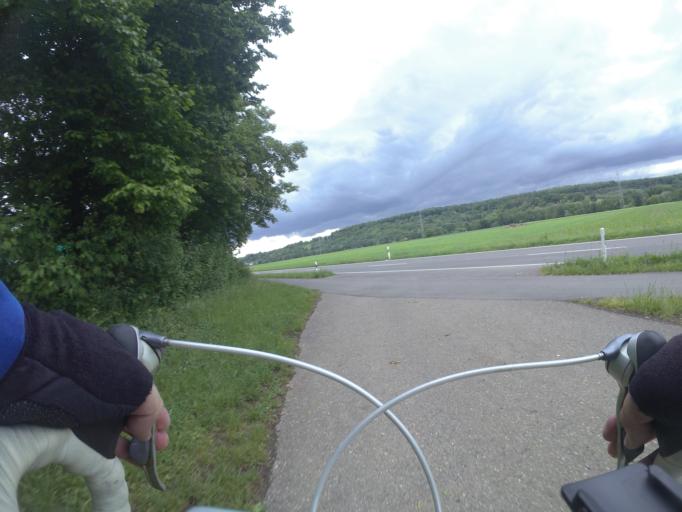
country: DE
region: Baden-Wuerttemberg
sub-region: Regierungsbezirk Stuttgart
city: Holzmaden
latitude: 48.6404
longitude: 9.4937
